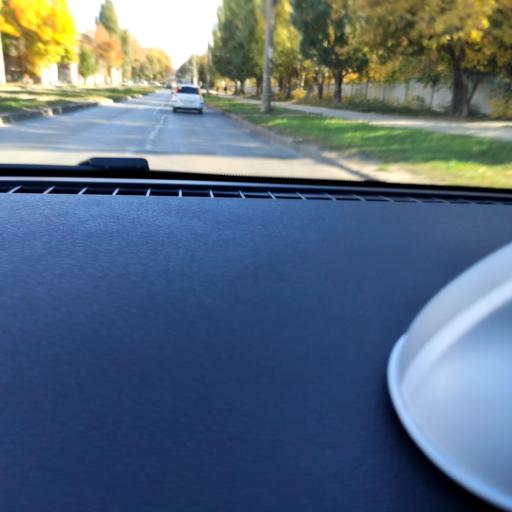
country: RU
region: Samara
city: Samara
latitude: 53.2215
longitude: 50.2317
